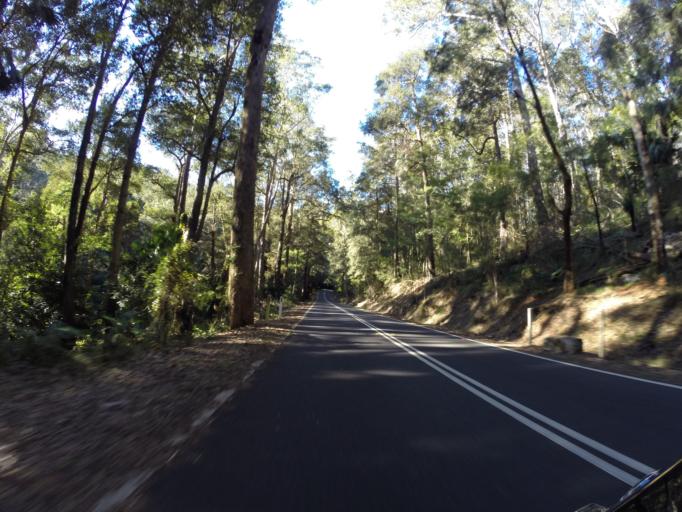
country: AU
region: New South Wales
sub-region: Wollongong
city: Helensburgh
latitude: -34.1511
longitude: 151.0250
